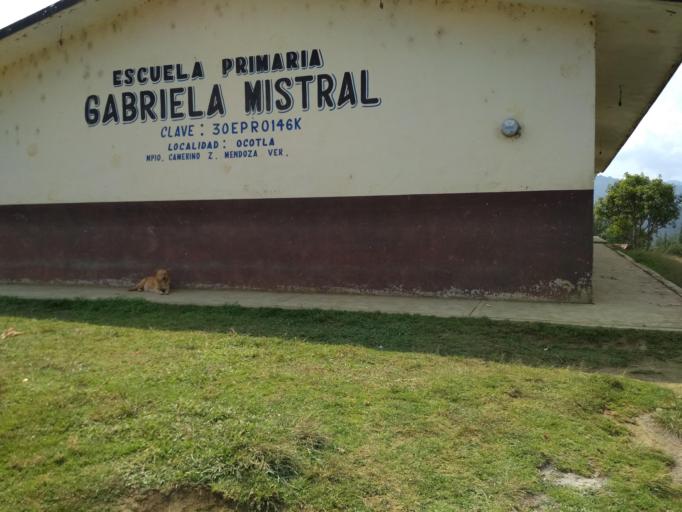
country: MX
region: Veracruz
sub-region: Camerino Z. Mendoza
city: Necoxtla
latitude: 18.7659
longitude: -97.1451
